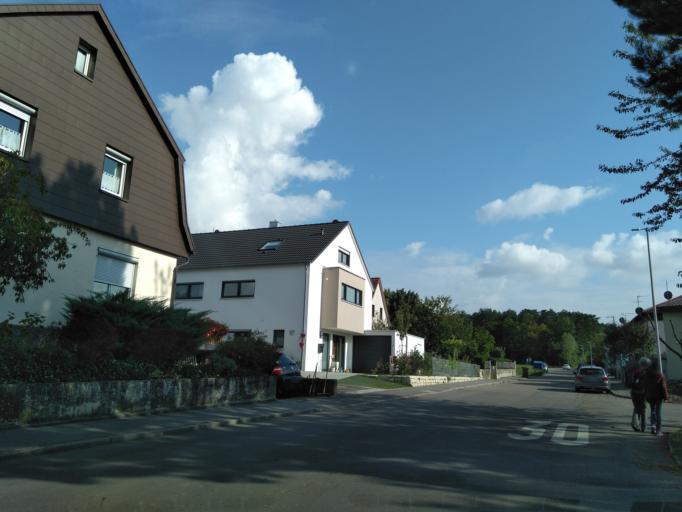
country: DE
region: Baden-Wuerttemberg
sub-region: Regierungsbezirk Stuttgart
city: Sersheim
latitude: 48.9562
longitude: 9.0194
